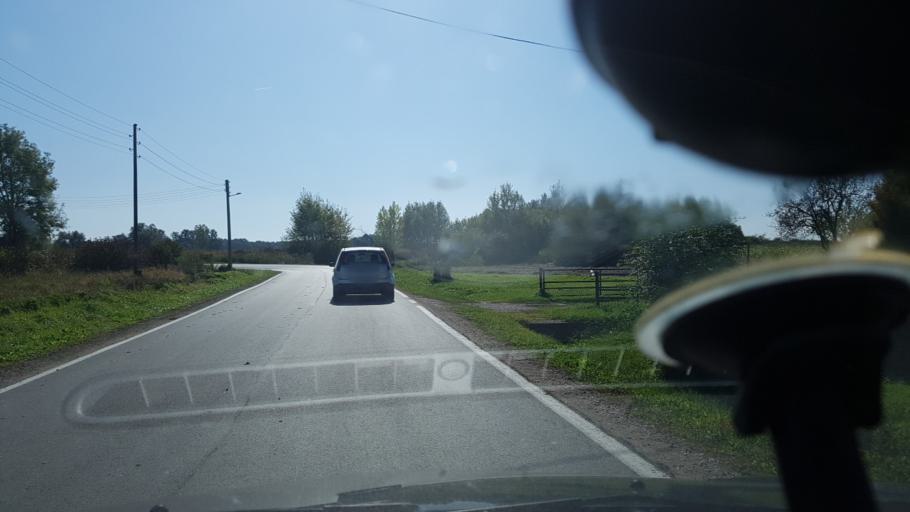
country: HR
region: Zagrebacka
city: Lupoglav
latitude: 45.7087
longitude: 16.3353
